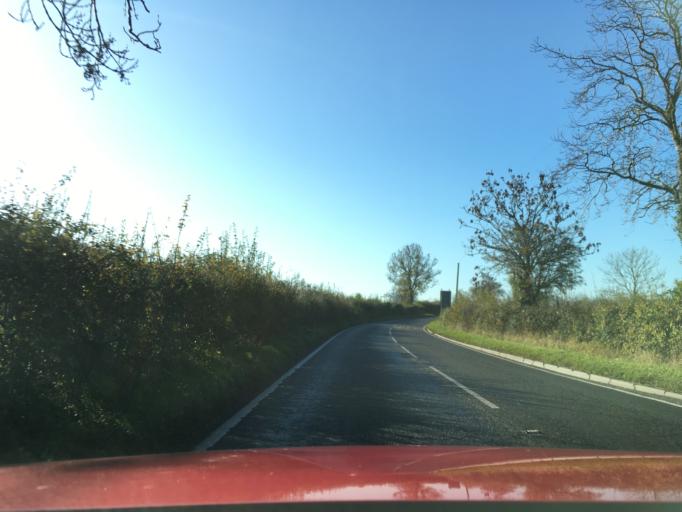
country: GB
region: England
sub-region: Somerset
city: Langport
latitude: 51.0744
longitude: -2.8530
